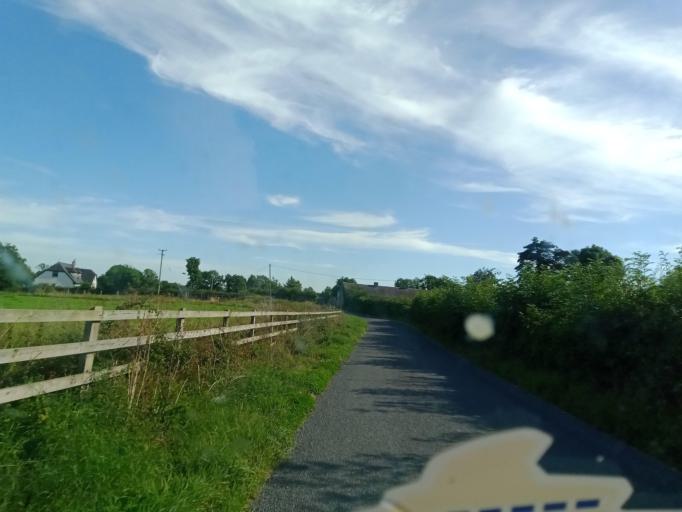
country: IE
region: Leinster
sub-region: Kilkenny
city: Ballyragget
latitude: 52.7759
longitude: -7.3891
